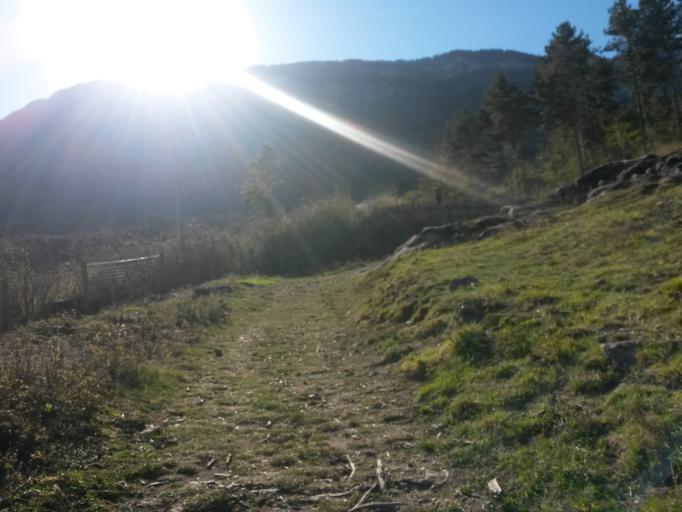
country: IT
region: Trentino-Alto Adige
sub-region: Bolzano
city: San Paolo
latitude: 46.4696
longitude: 11.2449
